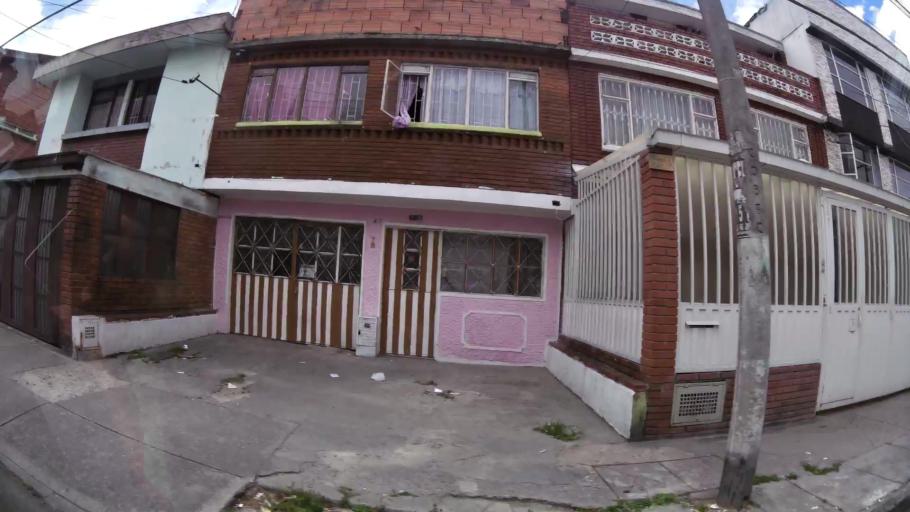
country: CO
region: Bogota D.C.
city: Bogota
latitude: 4.6015
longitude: -74.1085
